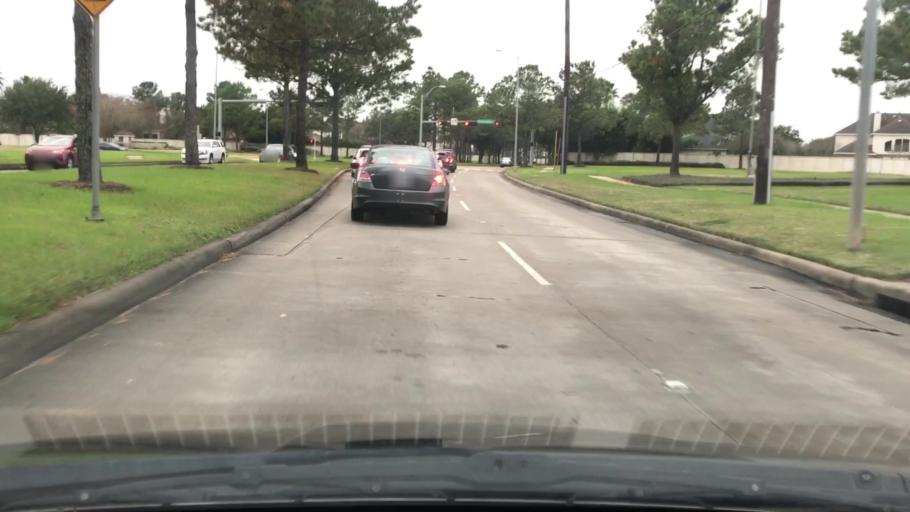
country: US
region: Texas
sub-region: Fort Bend County
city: Cinco Ranch
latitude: 29.7567
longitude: -95.7794
